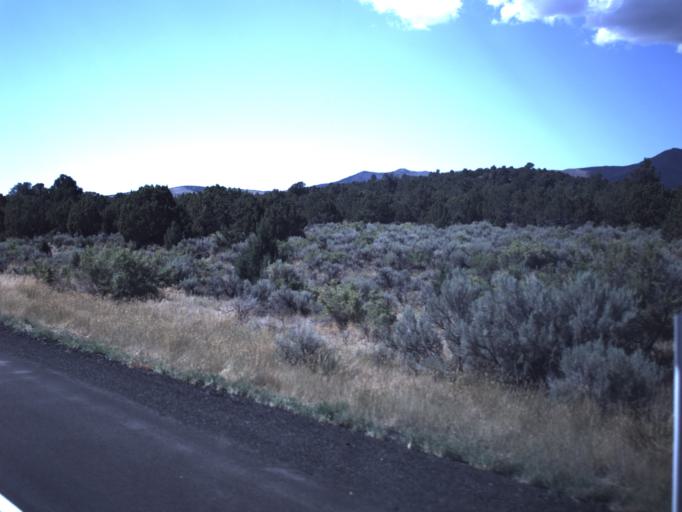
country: US
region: Utah
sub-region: Utah County
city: Eagle Mountain
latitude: 40.0069
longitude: -112.2760
